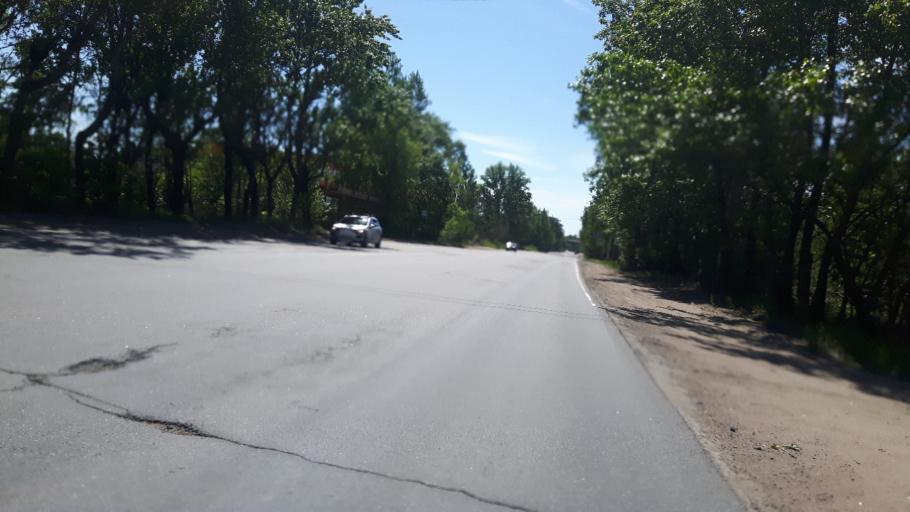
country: RU
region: Leningrad
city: Sosnovyy Bor
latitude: 59.8687
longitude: 29.0772
